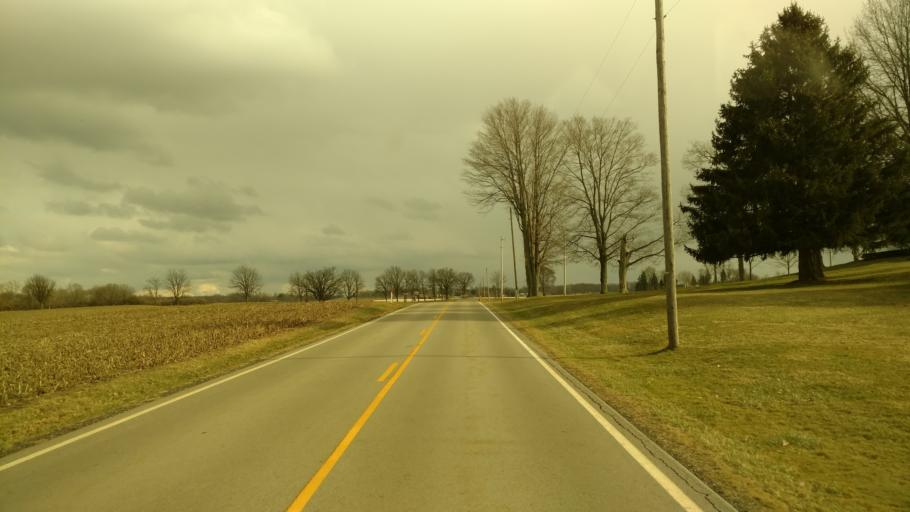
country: US
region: Ohio
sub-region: Crawford County
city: Galion
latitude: 40.7214
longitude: -82.7350
